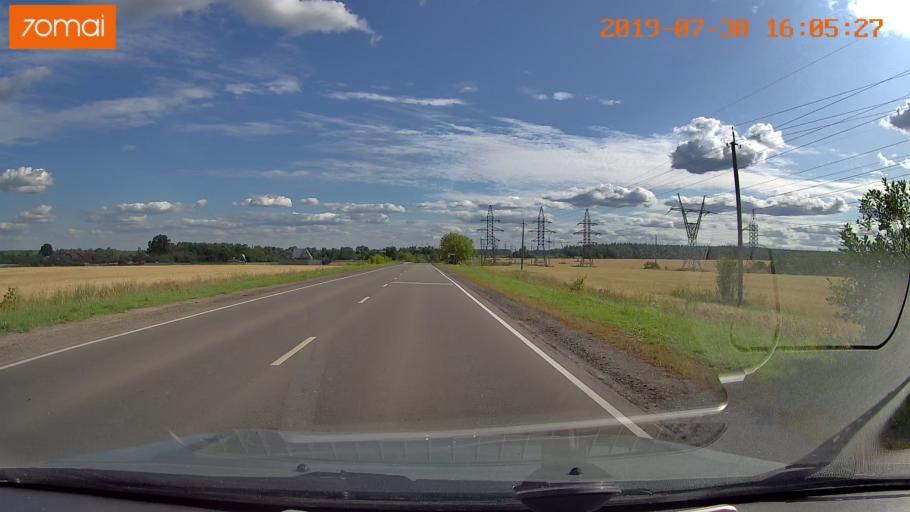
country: RU
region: Moskovskaya
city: Peski
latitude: 55.2654
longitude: 38.7150
